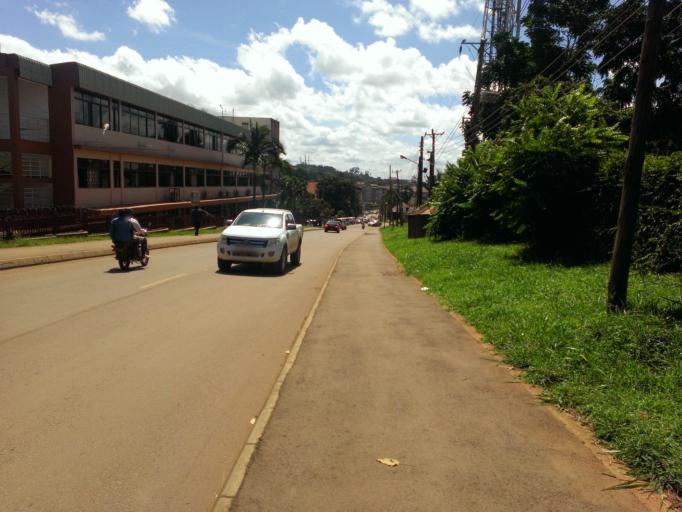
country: UG
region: Central Region
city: Kampala Central Division
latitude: 0.3260
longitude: 32.5766
